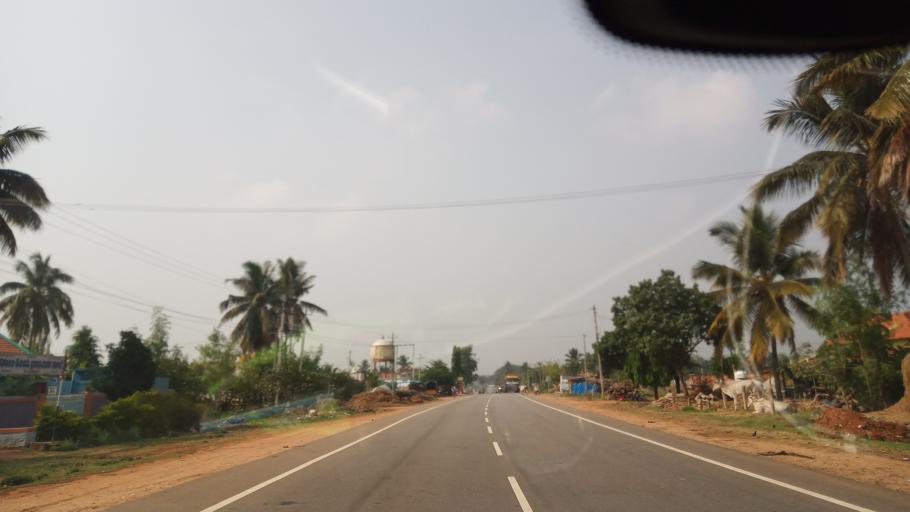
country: IN
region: Karnataka
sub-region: Mandya
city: Pandavapura
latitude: 12.5519
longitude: 76.6720
